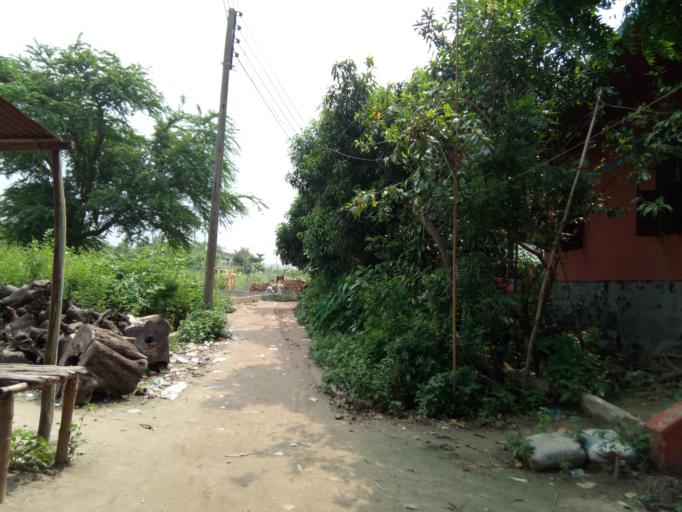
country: BD
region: Dhaka
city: Paltan
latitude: 23.7590
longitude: 90.4527
